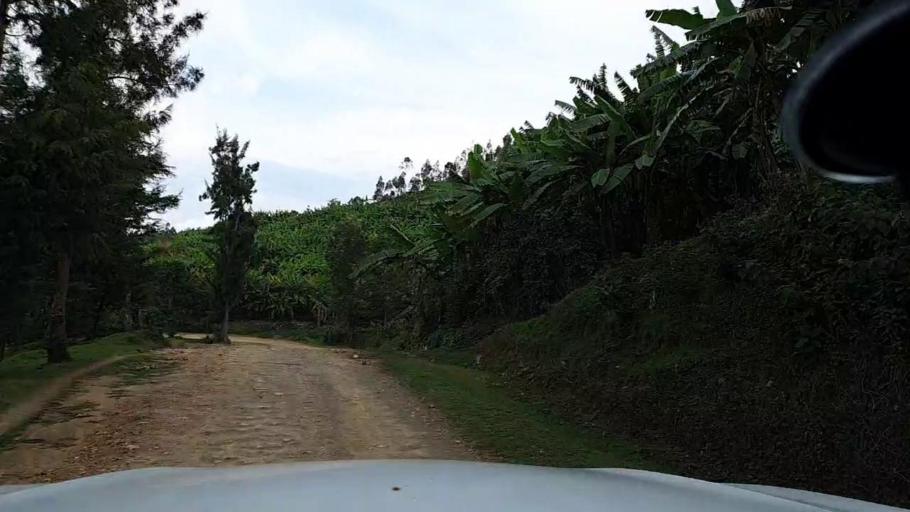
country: RW
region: Western Province
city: Kibuye
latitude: -2.1518
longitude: 29.5364
